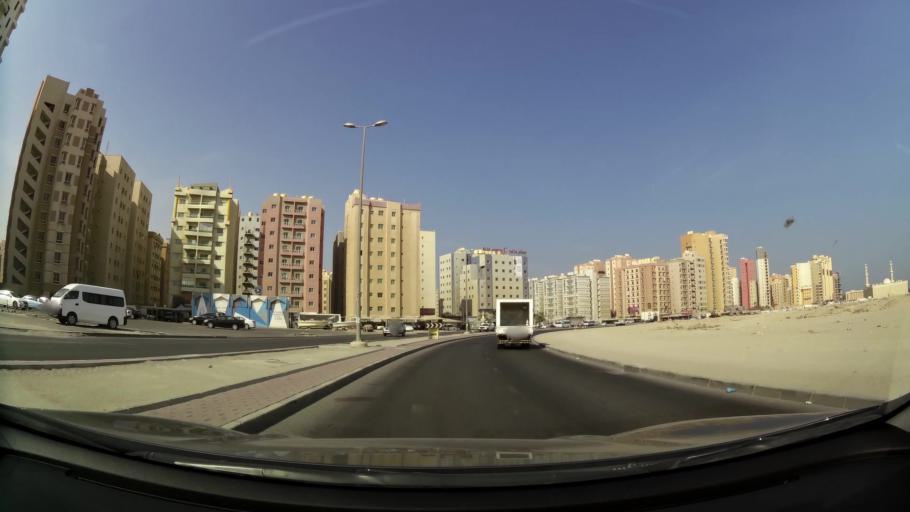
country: KW
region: Al Ahmadi
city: Al Mahbulah
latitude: 29.1435
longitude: 48.1203
